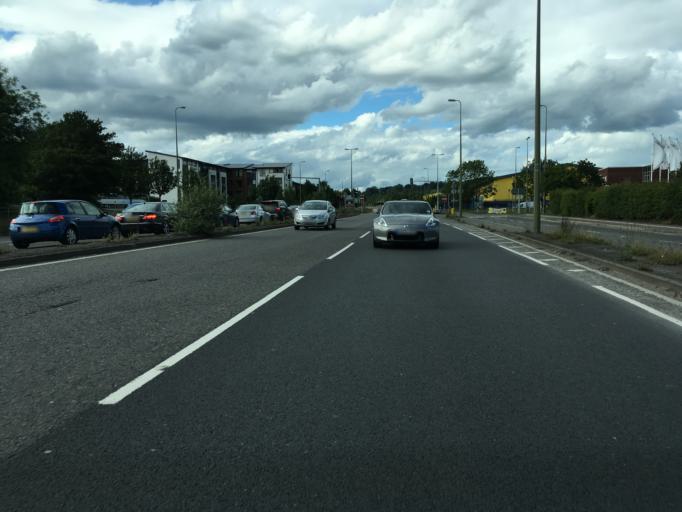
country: GB
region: England
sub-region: Oxfordshire
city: Cowley
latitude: 51.7364
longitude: -1.1978
